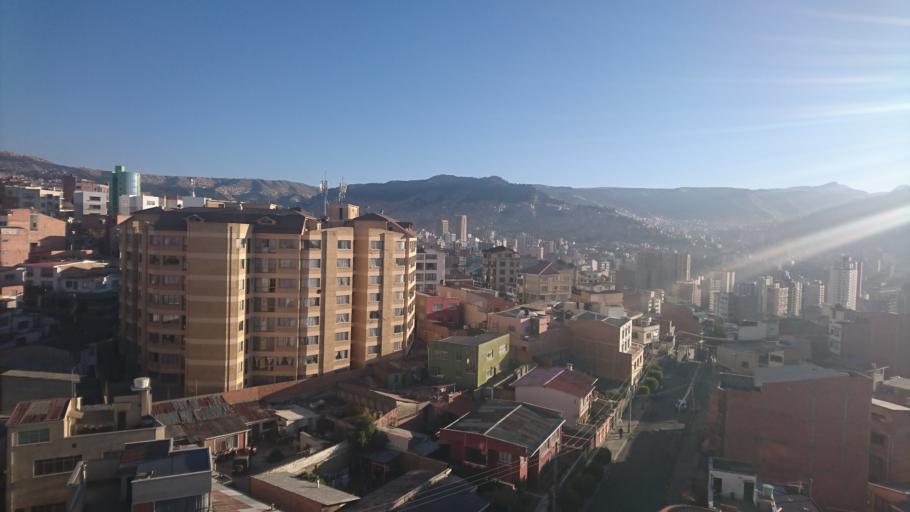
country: BO
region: La Paz
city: La Paz
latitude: -16.5148
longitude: -68.1325
